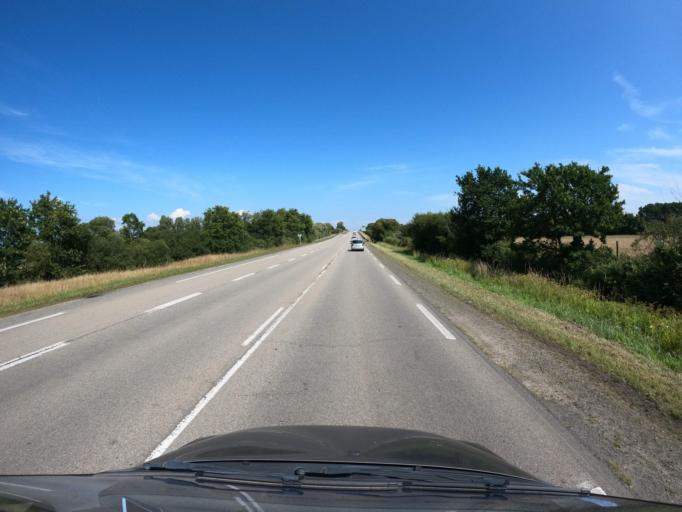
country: FR
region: Pays de la Loire
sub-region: Departement de la Loire-Atlantique
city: La Bernerie-en-Retz
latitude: 47.1059
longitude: -2.0546
